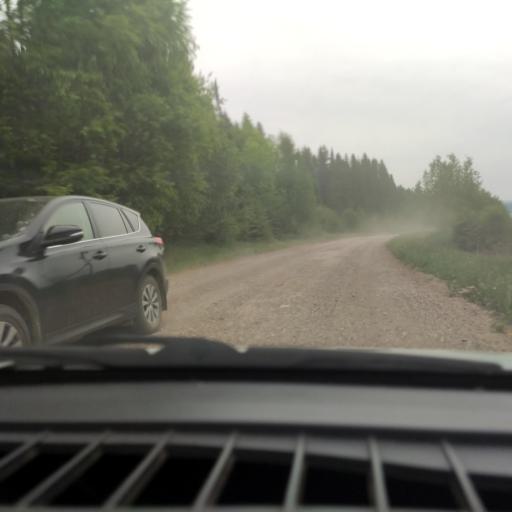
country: RU
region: Perm
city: Novyye Lyady
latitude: 57.9172
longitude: 56.6606
